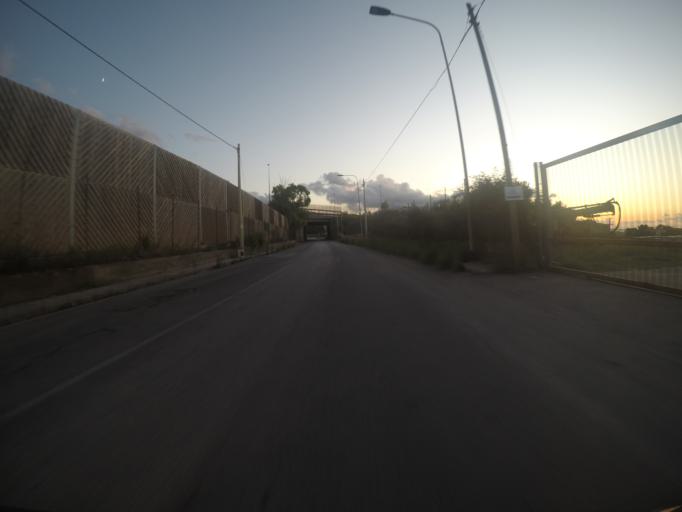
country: IT
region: Sicily
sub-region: Palermo
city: Isola delle Femmine
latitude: 38.1826
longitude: 13.2406
